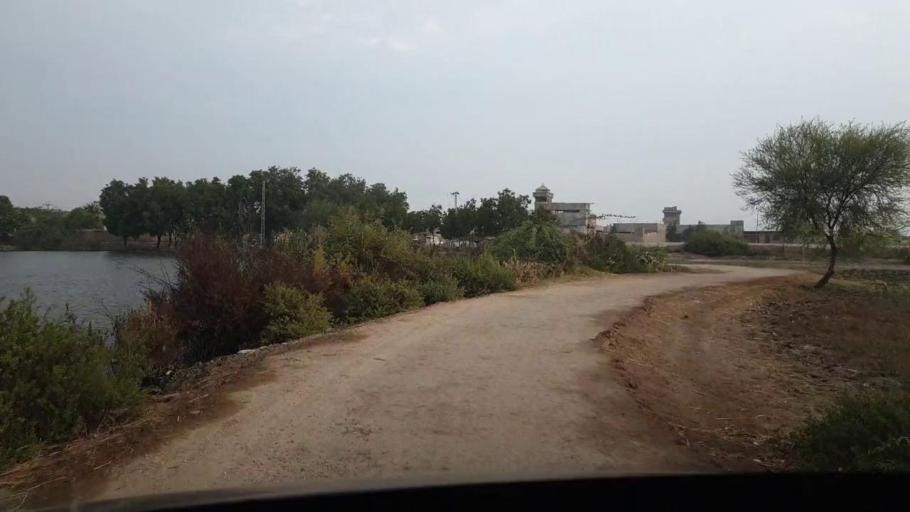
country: PK
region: Sindh
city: Thatta
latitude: 24.5978
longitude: 68.0822
